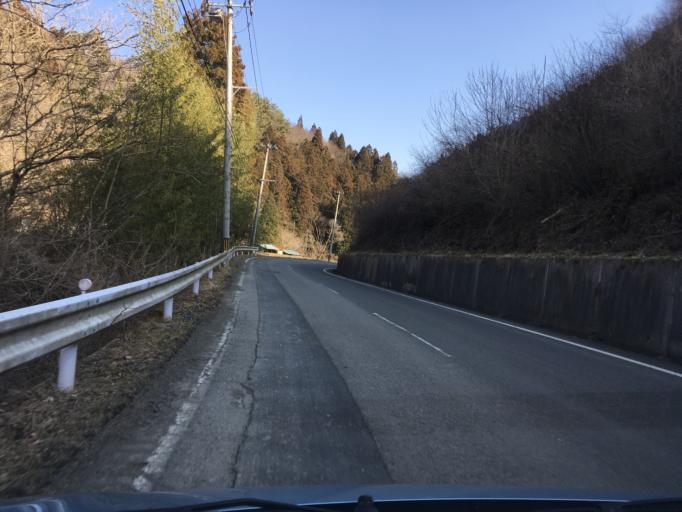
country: JP
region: Iwate
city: Ichinoseki
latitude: 38.7898
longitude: 141.4514
